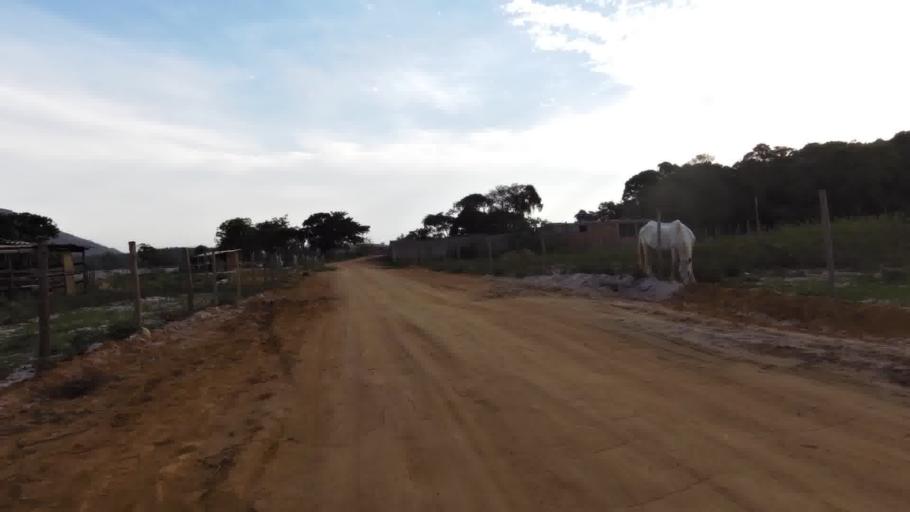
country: BR
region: Espirito Santo
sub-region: Piuma
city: Piuma
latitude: -20.8430
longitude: -40.7535
